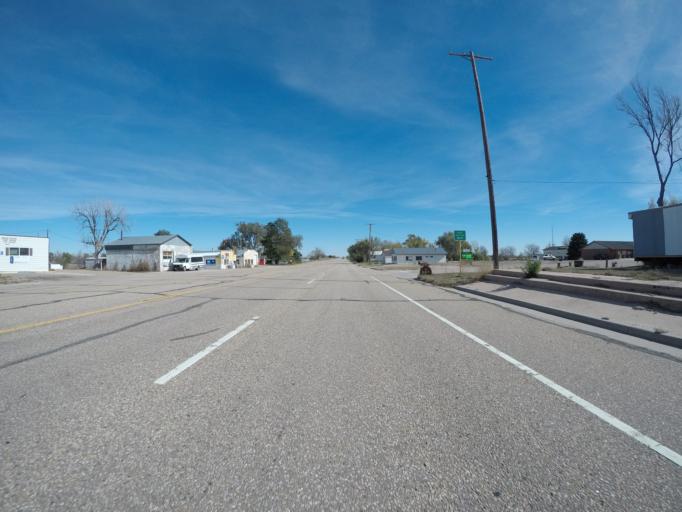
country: US
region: Colorado
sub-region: Yuma County
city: Yuma
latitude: 39.6559
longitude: -102.6796
